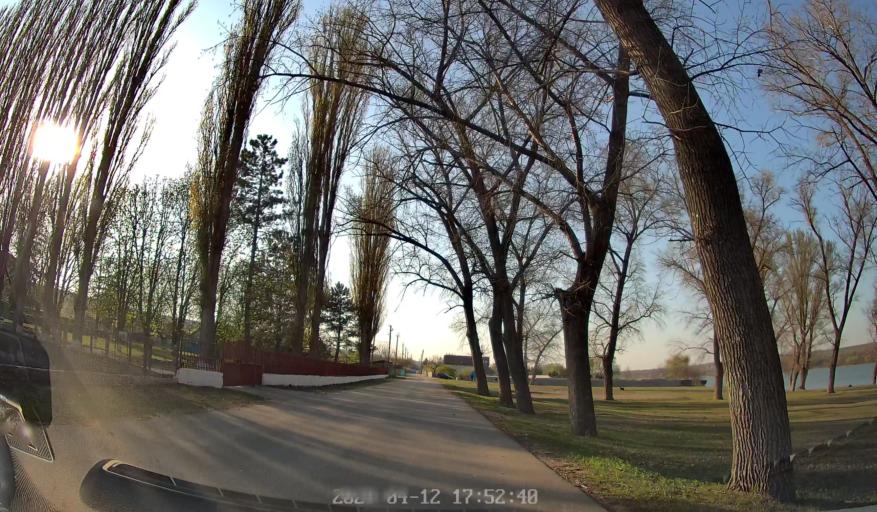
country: MD
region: Telenesti
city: Cocieri
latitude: 47.3828
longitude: 29.1245
